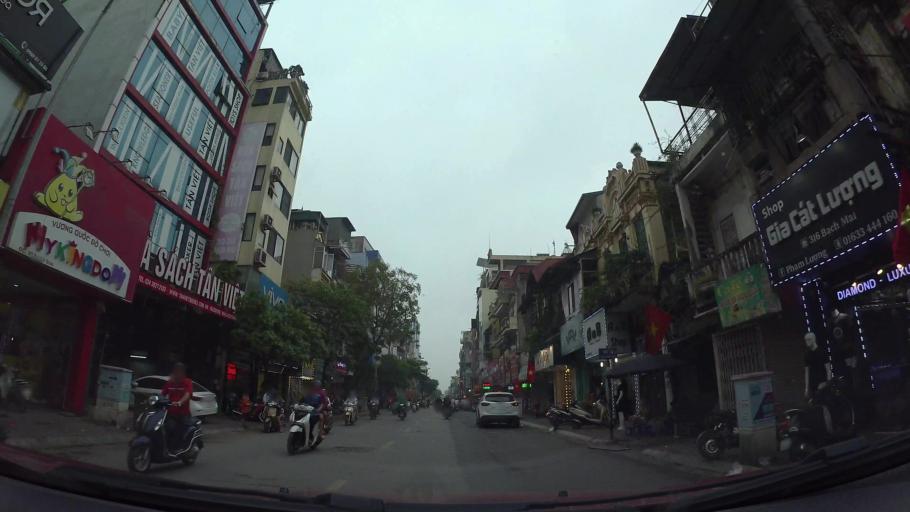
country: VN
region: Ha Noi
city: Hai BaTrung
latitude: 21.0015
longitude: 105.8507
